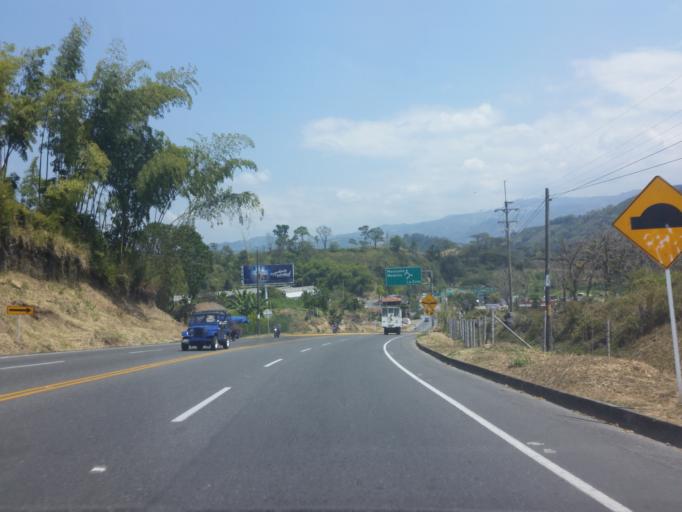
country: CO
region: Caldas
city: Chinchina
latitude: 4.9921
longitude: -75.6042
